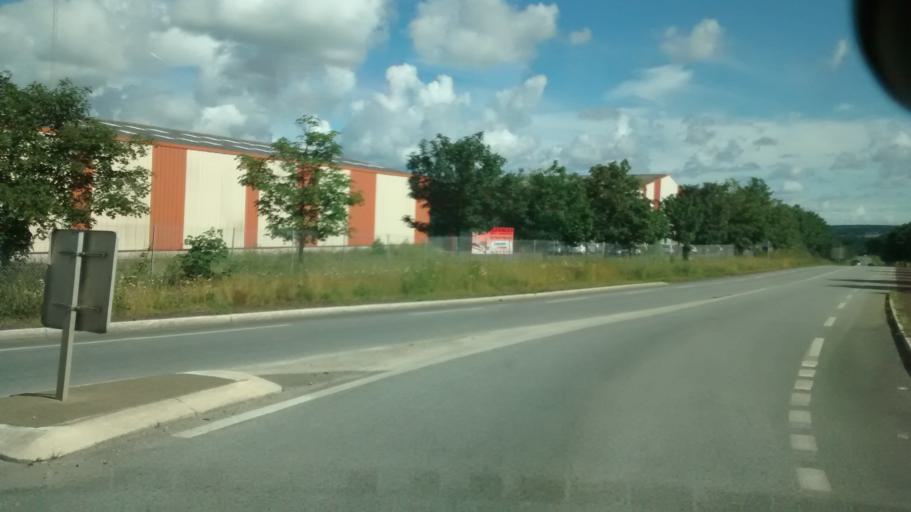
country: FR
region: Brittany
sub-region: Departement du Morbihan
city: Malestroit
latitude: 47.8503
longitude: -2.4192
